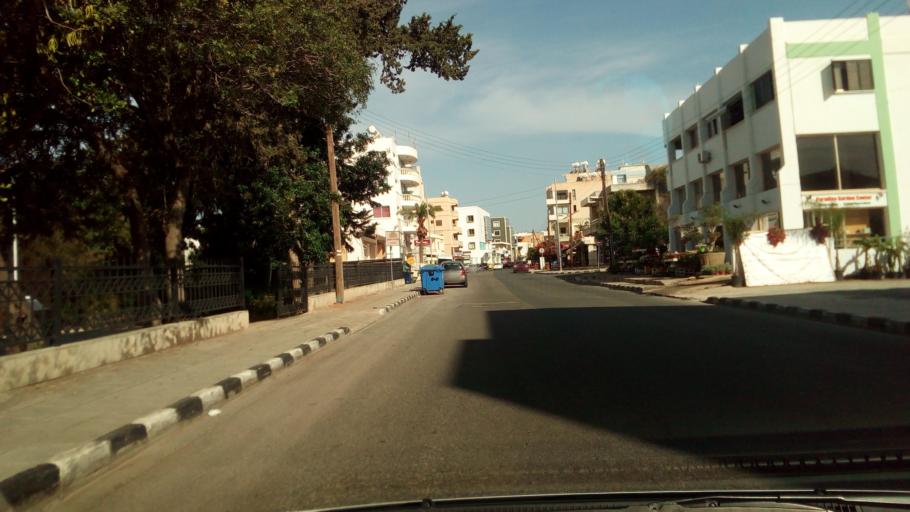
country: CY
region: Pafos
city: Paphos
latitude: 34.7724
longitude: 32.4310
